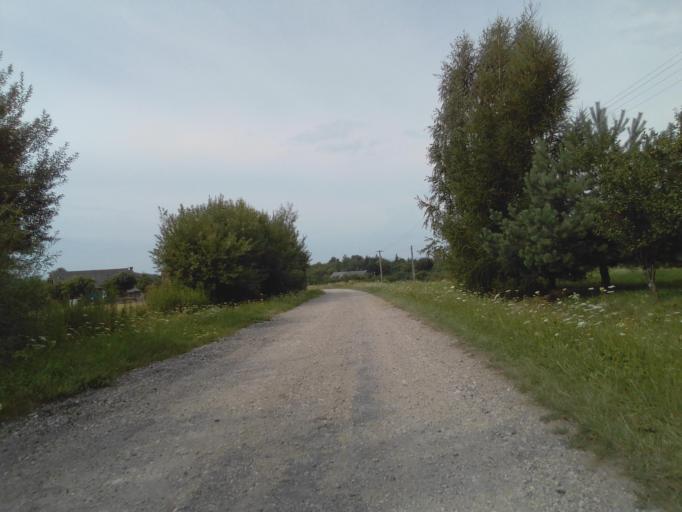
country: PL
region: Subcarpathian Voivodeship
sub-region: Powiat strzyzowski
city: Frysztak
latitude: 49.8790
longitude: 21.5336
